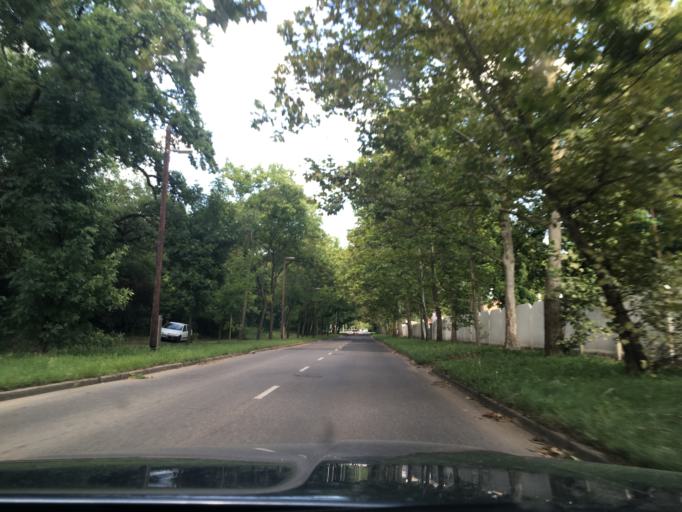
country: HU
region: Hajdu-Bihar
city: Debrecen
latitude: 47.5612
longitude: 21.6273
